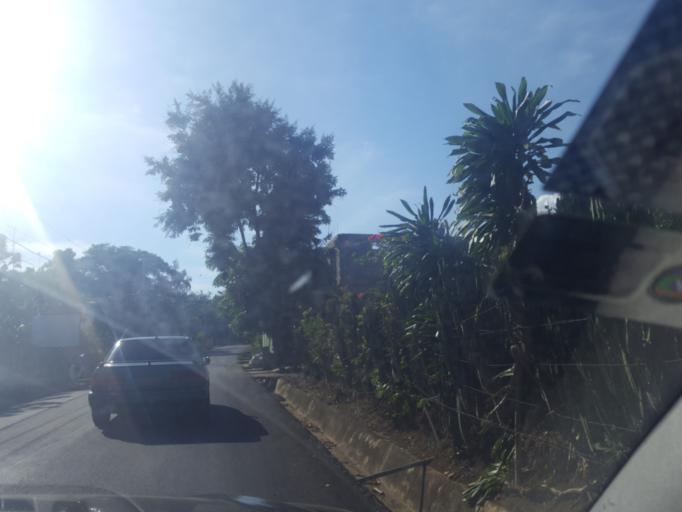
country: DO
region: La Vega
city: Rio Verde Arriba
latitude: 19.3475
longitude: -70.6249
